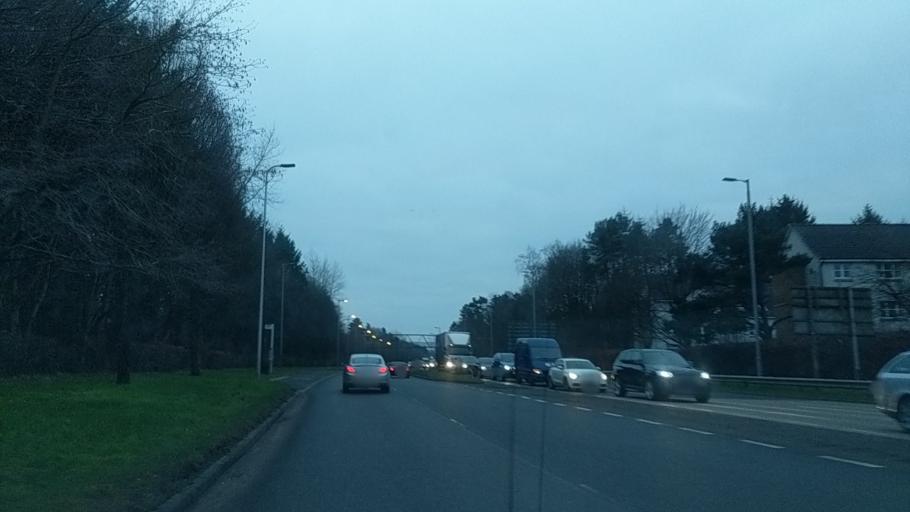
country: GB
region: Scotland
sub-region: South Lanarkshire
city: East Kilbride
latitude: 55.7749
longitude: -4.1632
